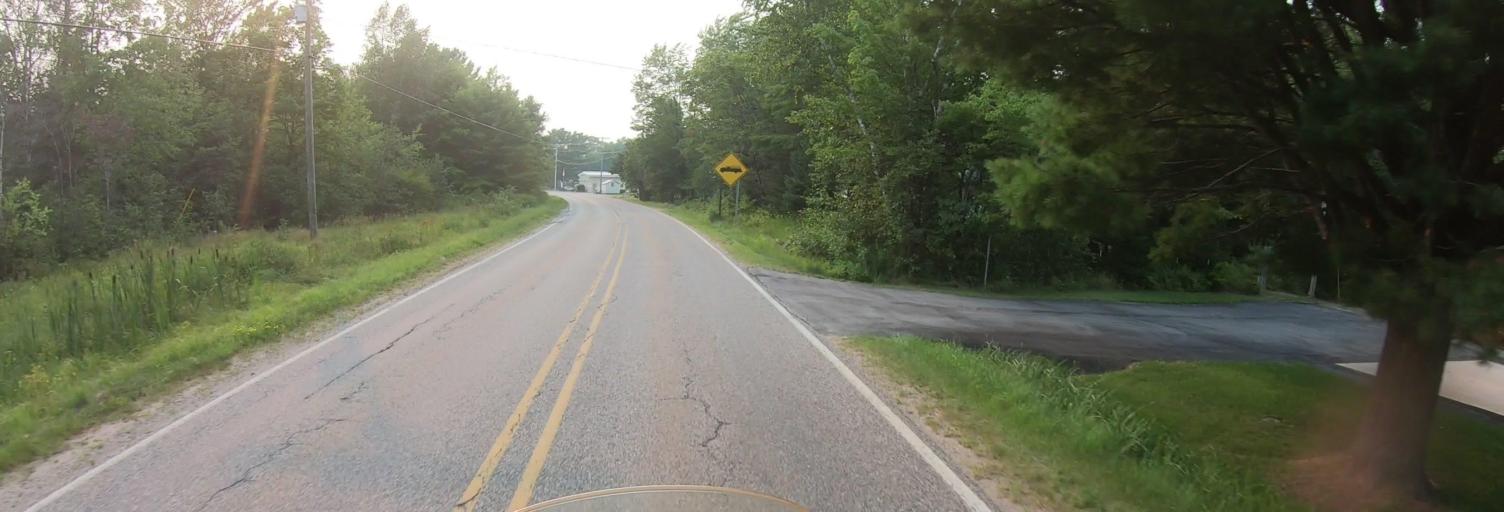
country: US
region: Michigan
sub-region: Chippewa County
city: Sault Ste. Marie
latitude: 46.4850
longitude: -84.6694
